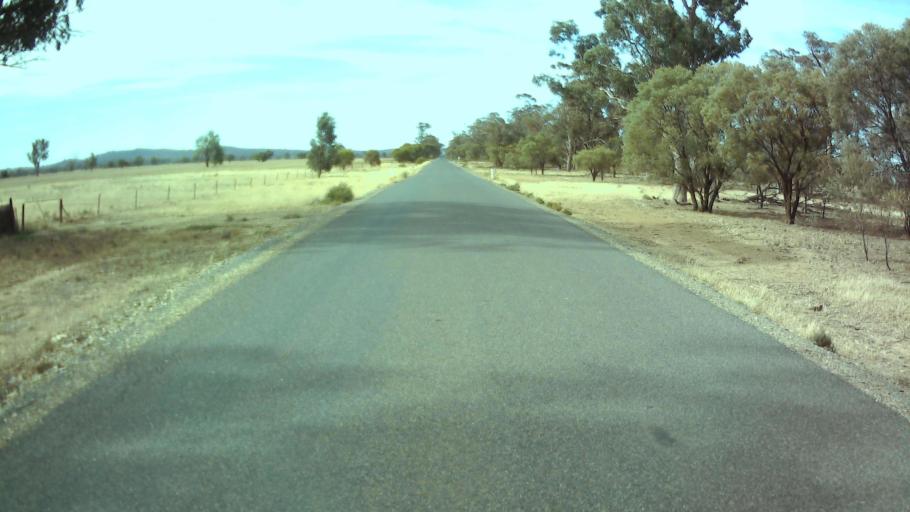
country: AU
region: New South Wales
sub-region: Weddin
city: Grenfell
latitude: -33.8743
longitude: 147.8574
